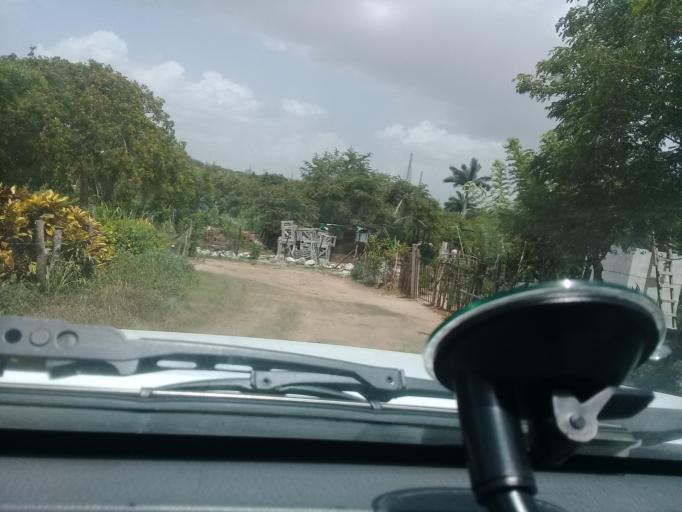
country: MX
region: Veracruz
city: Anahuac
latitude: 22.2225
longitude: -97.8270
